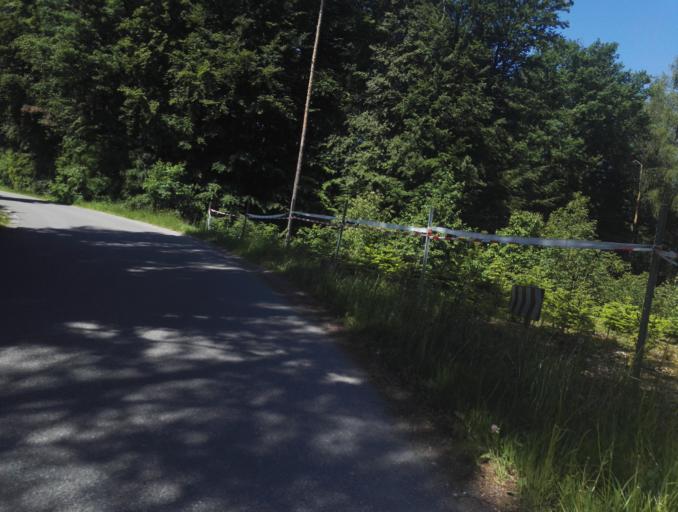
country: AT
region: Styria
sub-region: Politischer Bezirk Graz-Umgebung
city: Edelsgrub
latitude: 47.0505
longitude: 15.5618
